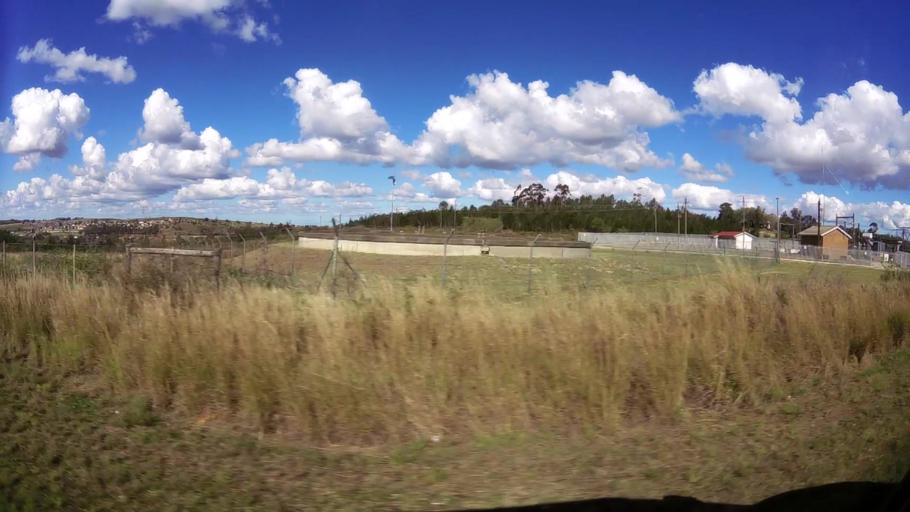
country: ZA
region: Western Cape
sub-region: Overberg District Municipality
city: Swellendam
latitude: -34.0249
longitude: 20.4271
